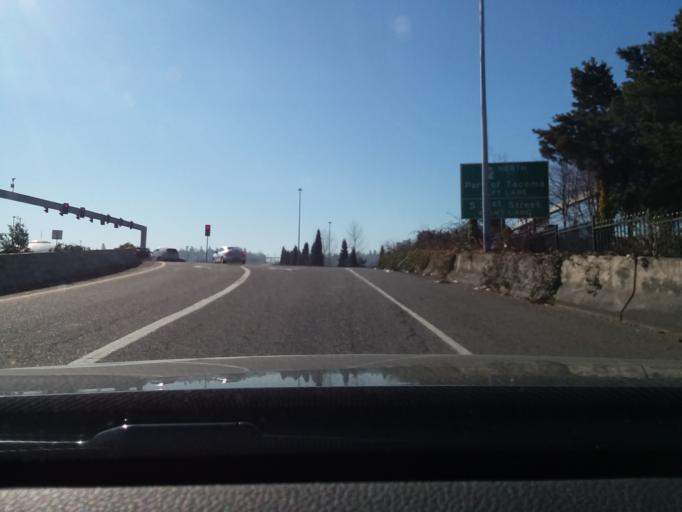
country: US
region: Washington
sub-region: Pierce County
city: Tacoma
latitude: 47.2438
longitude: -122.4352
